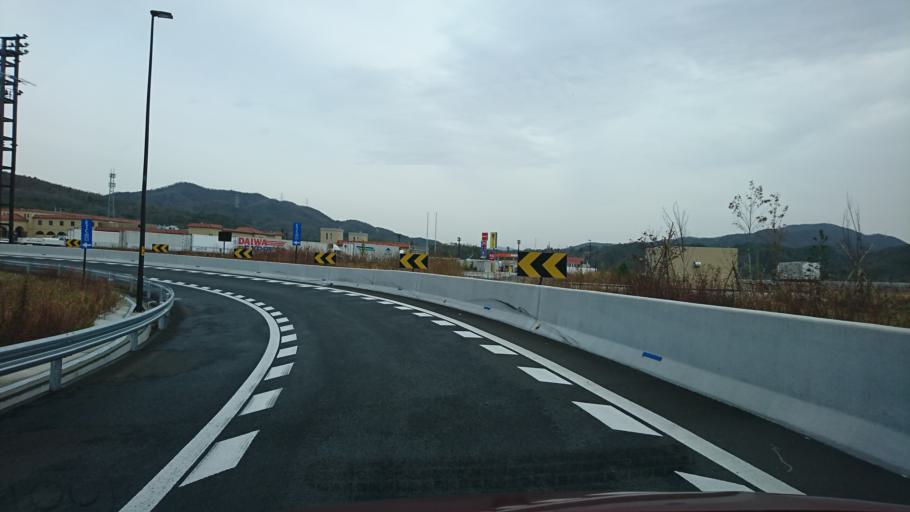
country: JP
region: Hyogo
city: Sandacho
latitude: 34.8651
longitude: 135.3022
